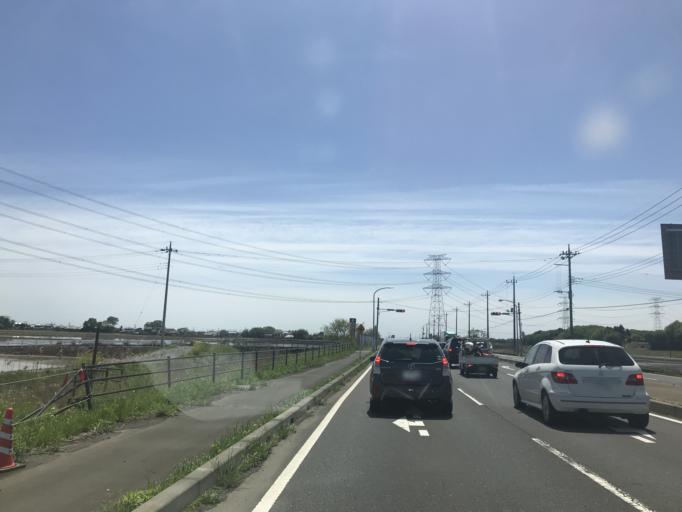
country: JP
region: Ibaraki
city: Shimodate
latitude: 36.2467
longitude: 139.9836
